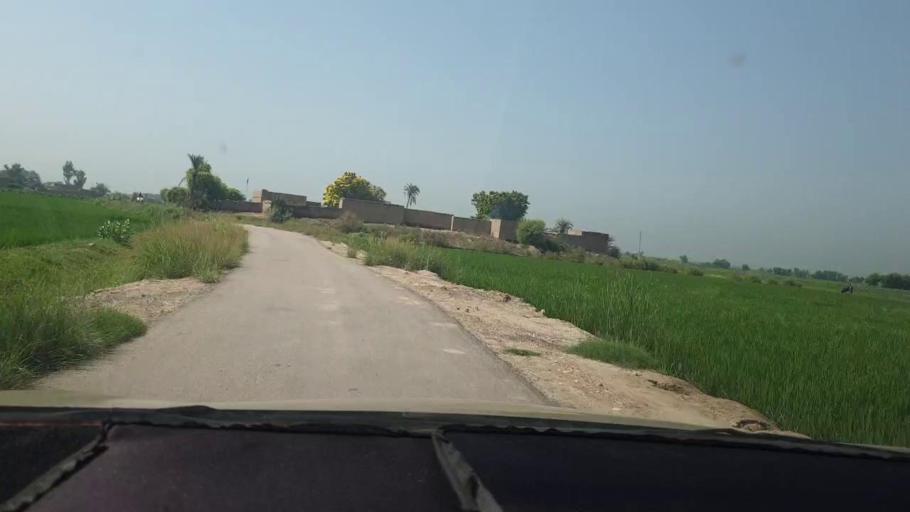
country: PK
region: Sindh
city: Kambar
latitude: 27.5620
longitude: 68.0440
